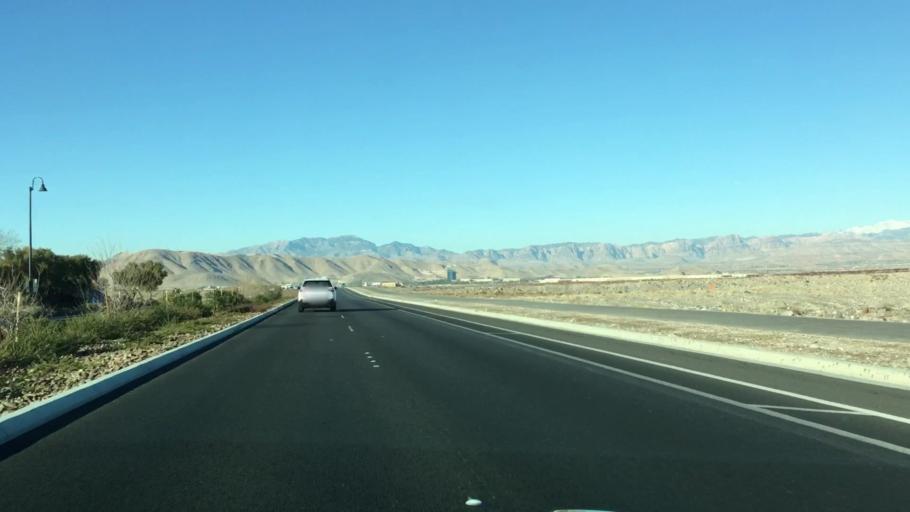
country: US
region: Nevada
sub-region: Clark County
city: Whitney
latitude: 35.9600
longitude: -115.1289
